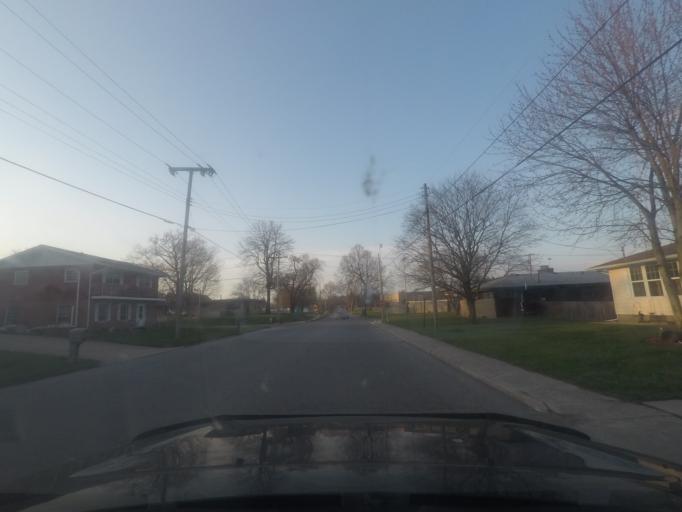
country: US
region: Indiana
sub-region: LaPorte County
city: LaPorte
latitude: 41.5979
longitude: -86.7292
